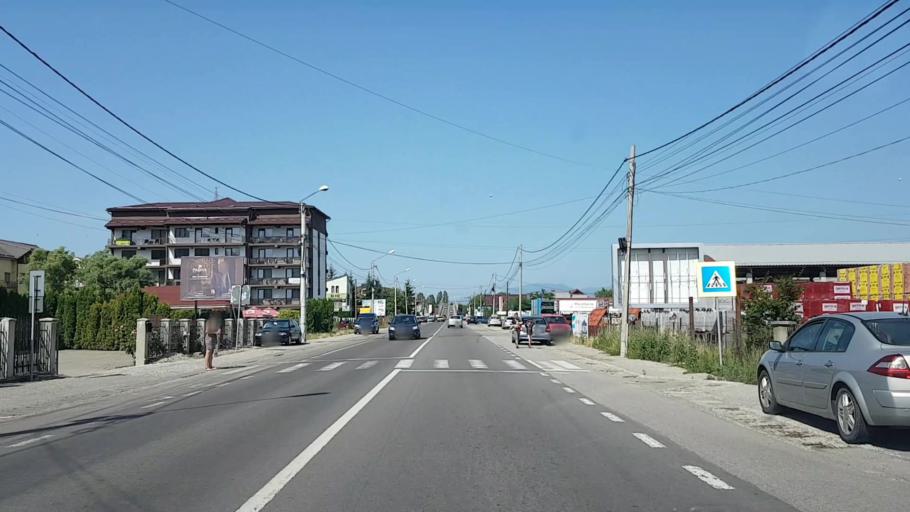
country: RO
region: Bistrita-Nasaud
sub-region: Municipiul Bistrita
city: Viisoara
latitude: 47.1123
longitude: 24.4605
